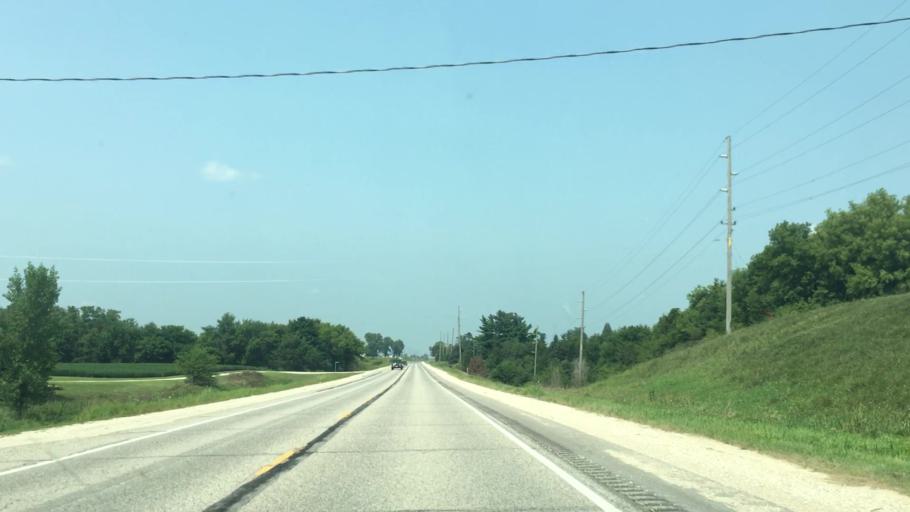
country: US
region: Iowa
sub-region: Fayette County
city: Fayette
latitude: 42.8742
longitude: -91.8104
